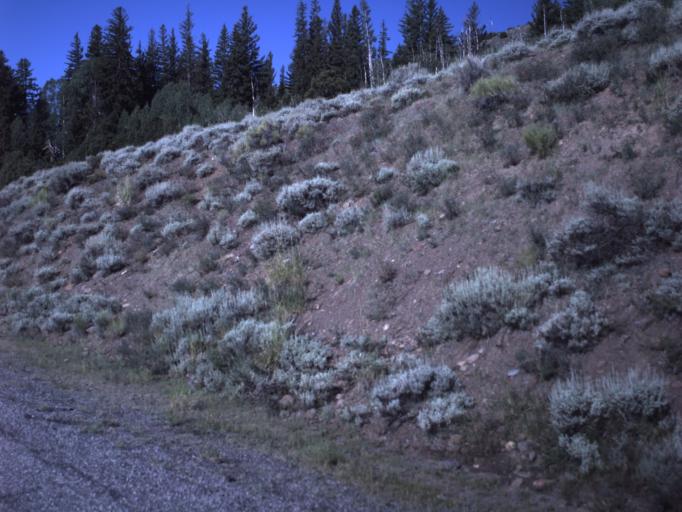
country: US
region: Utah
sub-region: Wayne County
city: Loa
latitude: 38.5949
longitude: -111.4700
